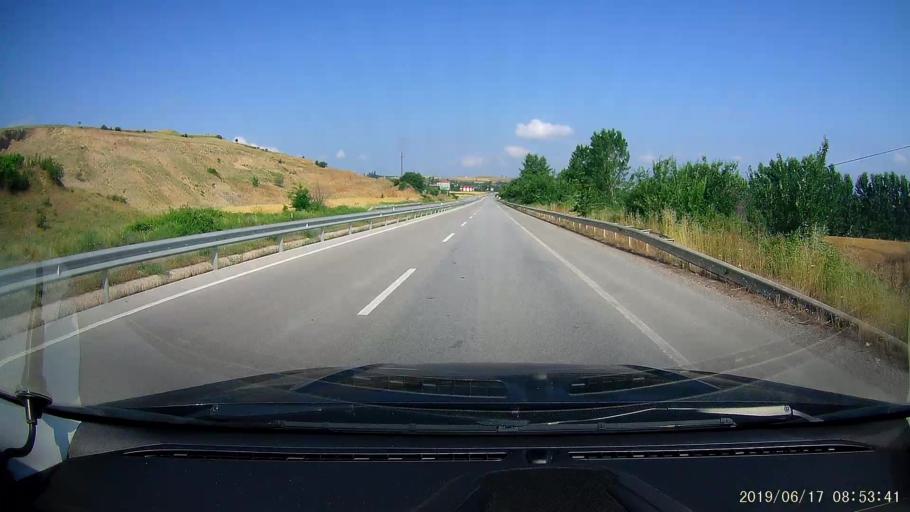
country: TR
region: Tokat
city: Erbaa
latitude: 40.7120
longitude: 36.4763
